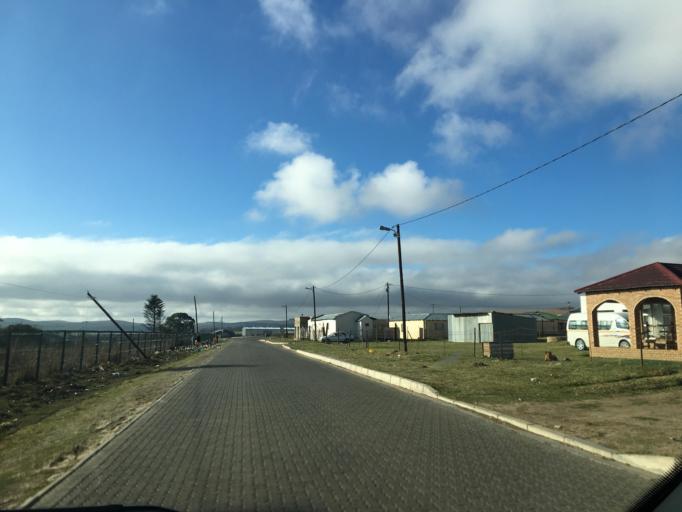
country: ZA
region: Eastern Cape
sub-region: Chris Hani District Municipality
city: Elliot
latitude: -31.3376
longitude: 27.8366
